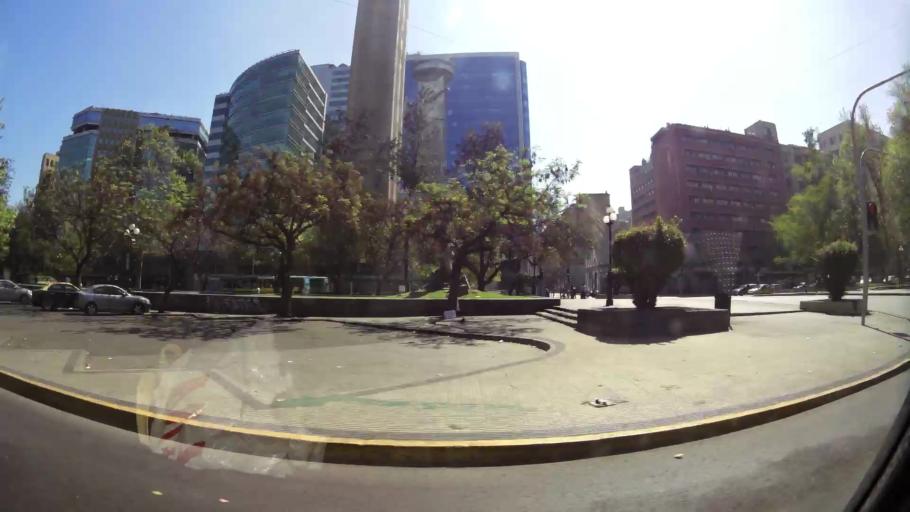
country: CL
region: Santiago Metropolitan
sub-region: Provincia de Santiago
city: Santiago
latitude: -33.4452
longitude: -70.6555
